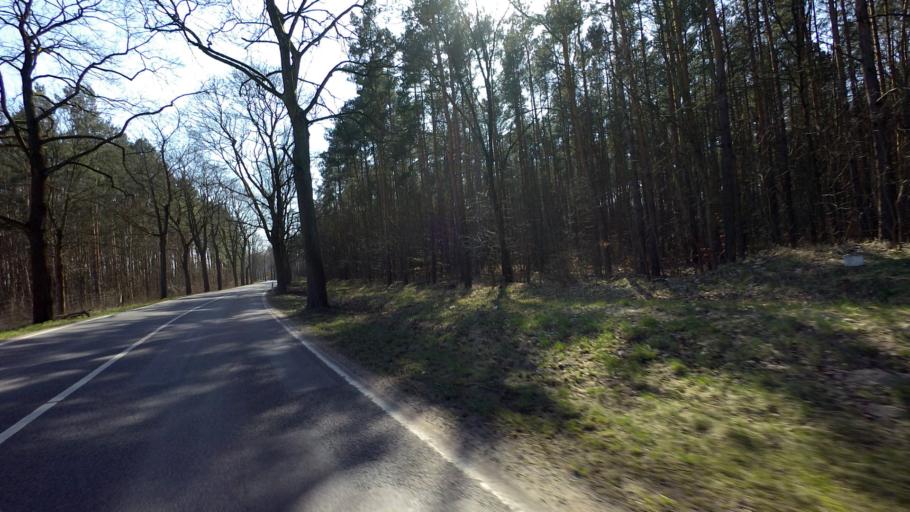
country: DE
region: Brandenburg
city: Leegebruch
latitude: 52.7285
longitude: 13.1802
